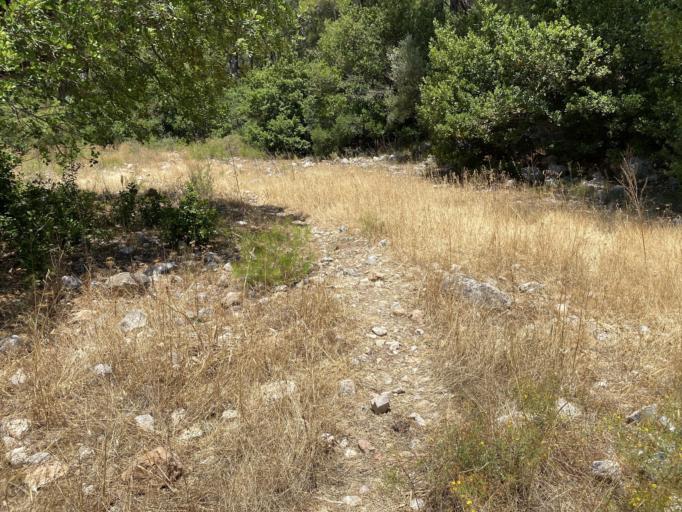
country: TR
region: Antalya
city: Tekirova
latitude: 36.3976
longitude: 30.4701
